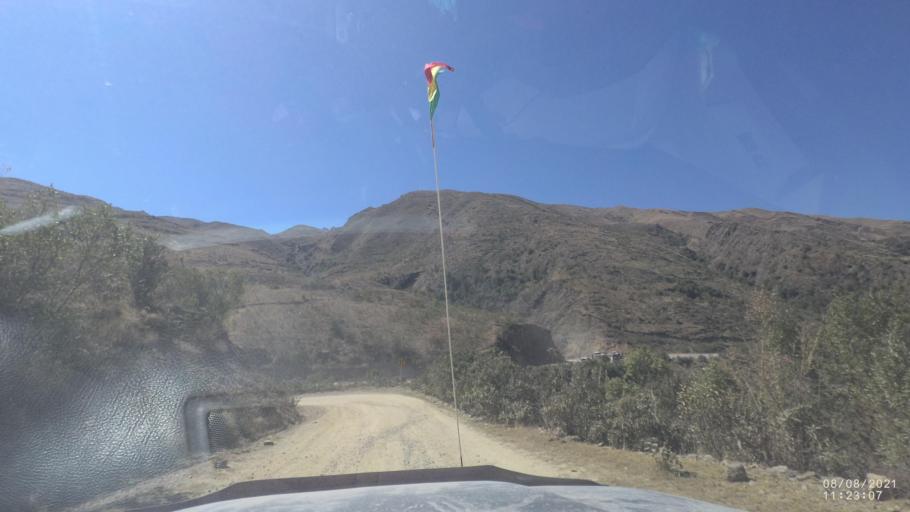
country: BO
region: Cochabamba
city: Colchani
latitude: -16.7772
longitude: -66.6460
